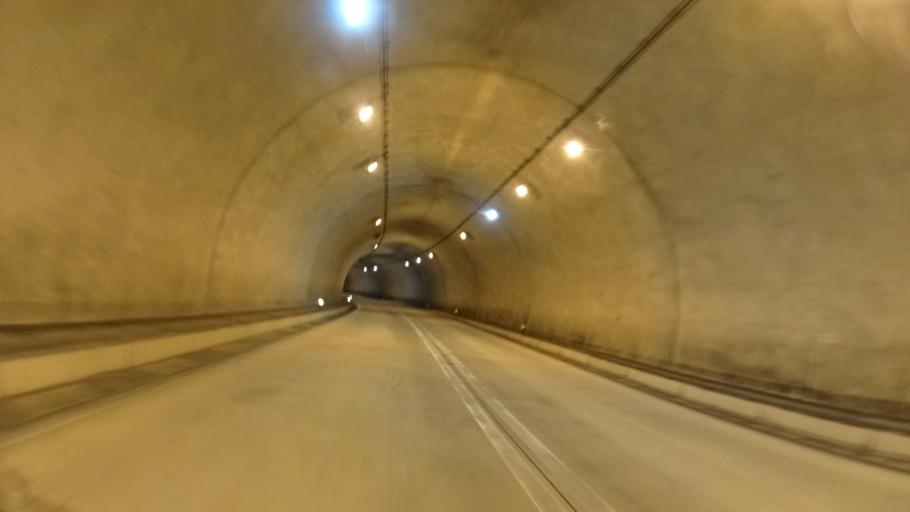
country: JP
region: Fukui
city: Maruoka
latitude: 36.1958
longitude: 136.3454
